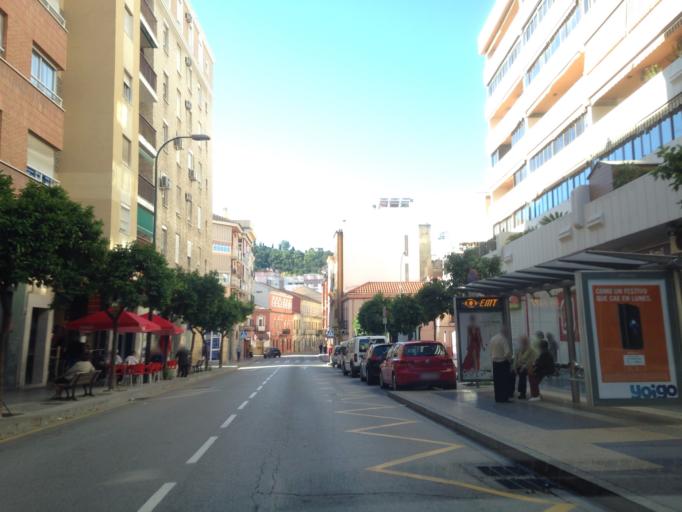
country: ES
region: Andalusia
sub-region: Provincia de Malaga
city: Malaga
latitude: 36.7296
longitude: -4.4148
